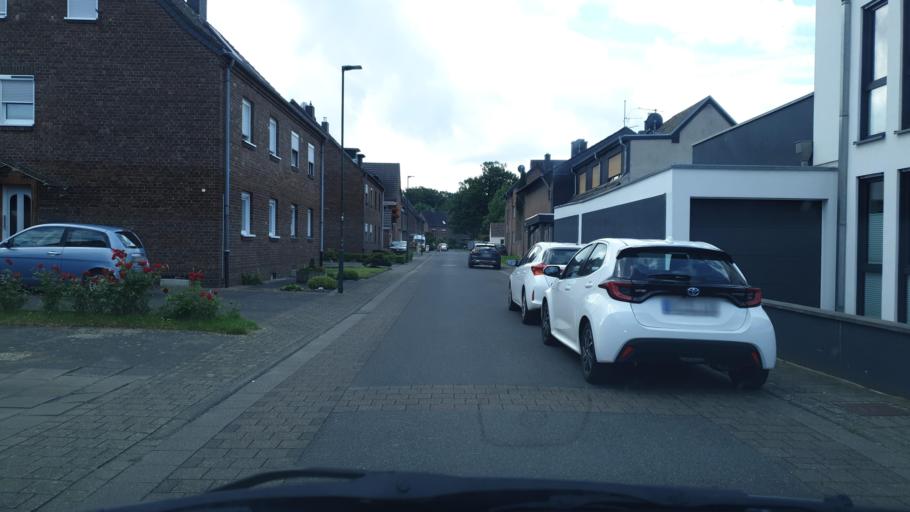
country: DE
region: North Rhine-Westphalia
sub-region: Regierungsbezirk Koln
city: Kerpen
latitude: 50.9174
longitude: 6.7275
